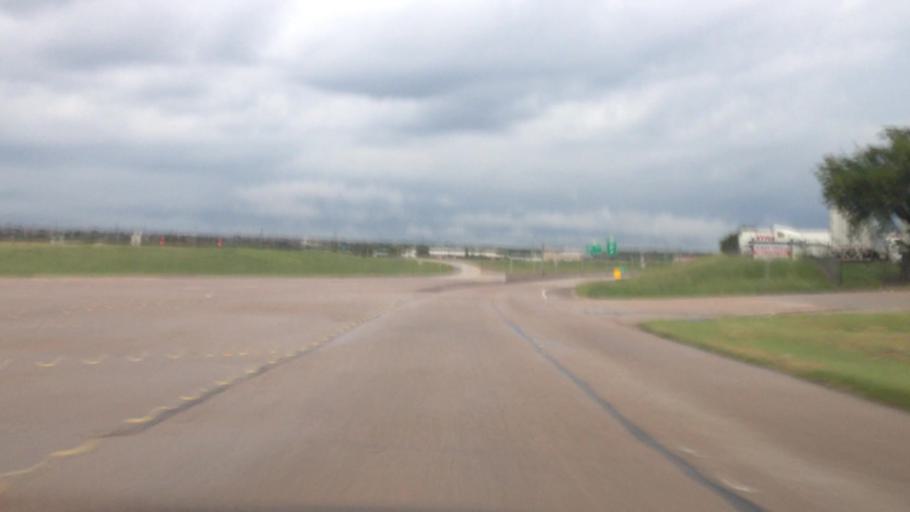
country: US
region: Texas
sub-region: Tarrant County
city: Saginaw
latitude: 32.8317
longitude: -97.3602
